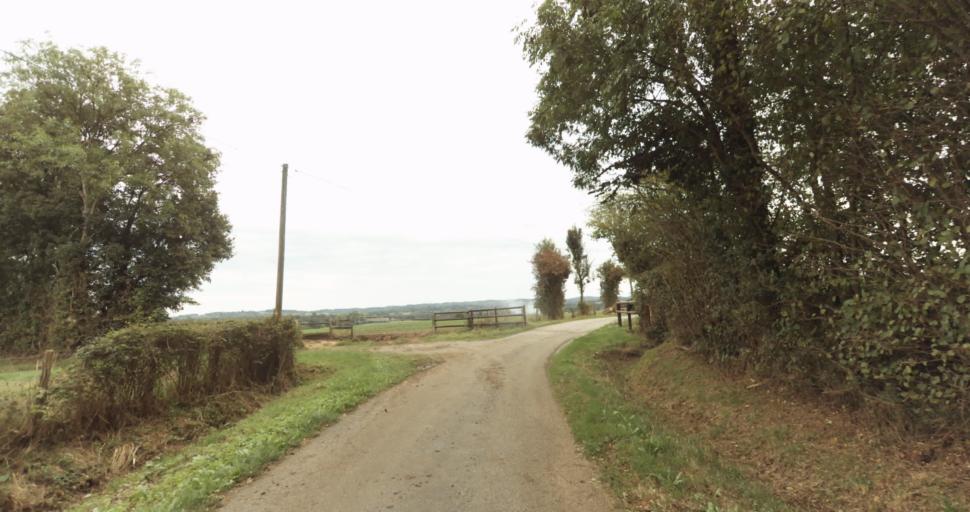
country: FR
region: Lower Normandy
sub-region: Departement de l'Orne
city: Sees
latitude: 48.6753
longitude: 0.2690
